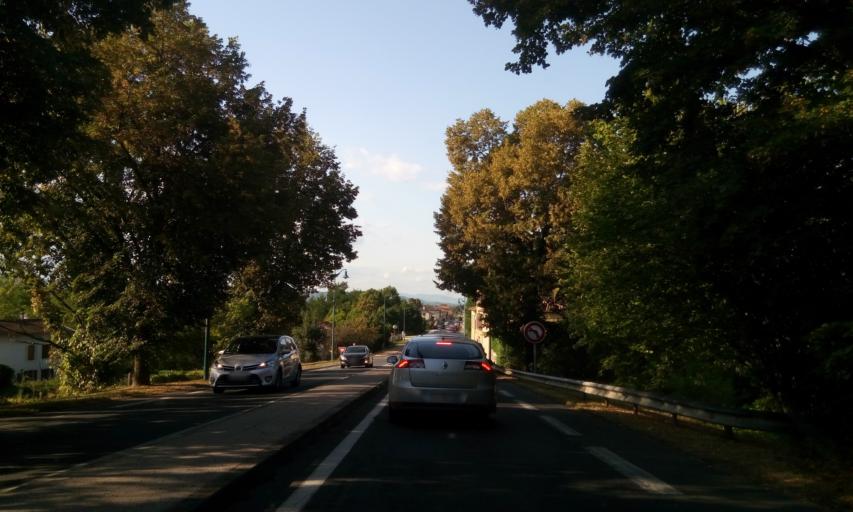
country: FR
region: Rhone-Alpes
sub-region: Departement du Rhone
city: Les Cheres
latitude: 45.8839
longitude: 4.7447
